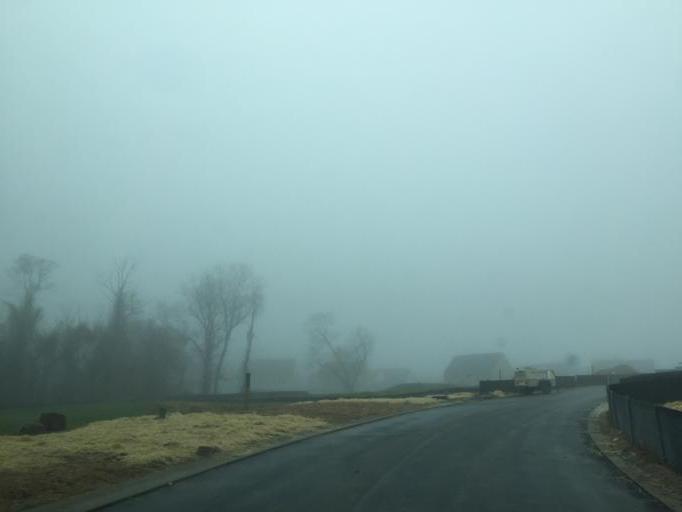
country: US
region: Maryland
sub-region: Howard County
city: Columbia
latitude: 39.2468
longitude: -76.8521
